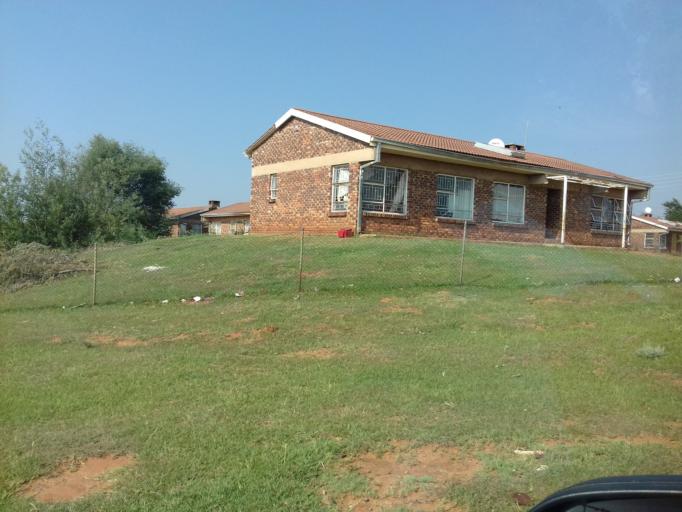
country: LS
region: Maseru
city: Maseru
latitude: -29.4517
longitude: 27.5632
